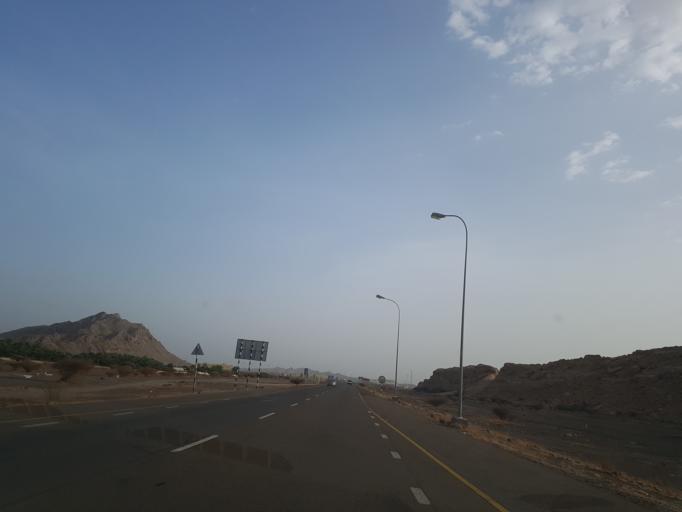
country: OM
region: Al Buraimi
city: Al Buraymi
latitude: 24.2285
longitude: 55.9572
